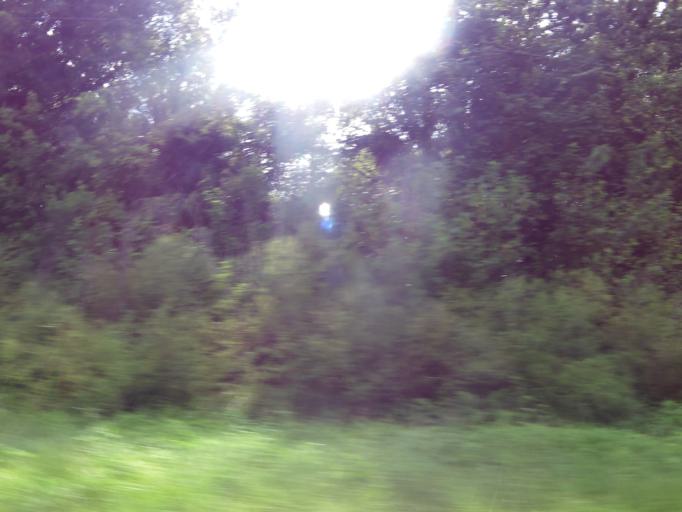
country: US
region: Florida
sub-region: Clay County
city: Green Cove Springs
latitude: 29.9733
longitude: -81.6931
